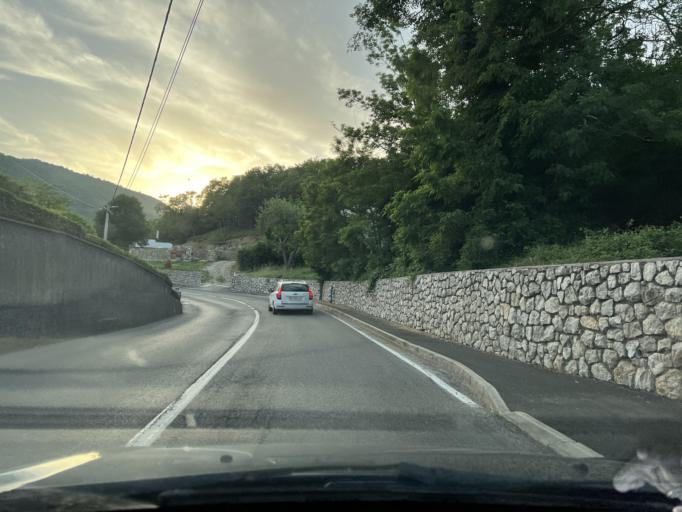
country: HR
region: Primorsko-Goranska
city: Drazice
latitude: 45.3926
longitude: 14.4315
